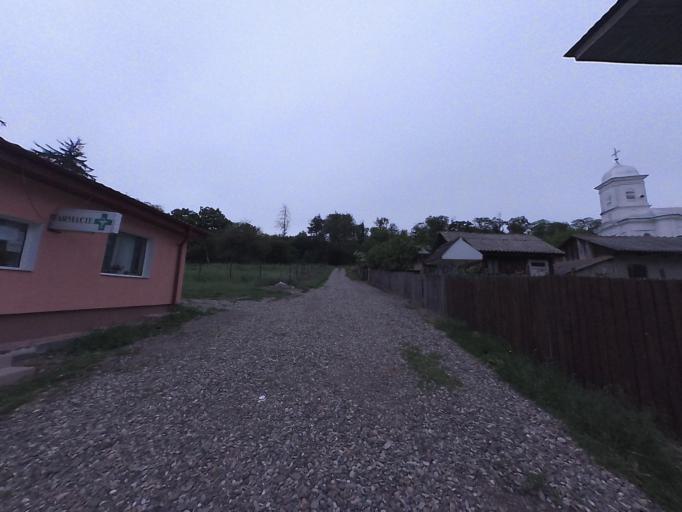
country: RO
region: Neamt
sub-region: Comuna Dulcesti
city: Dulcesti
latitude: 46.9666
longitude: 26.7846
